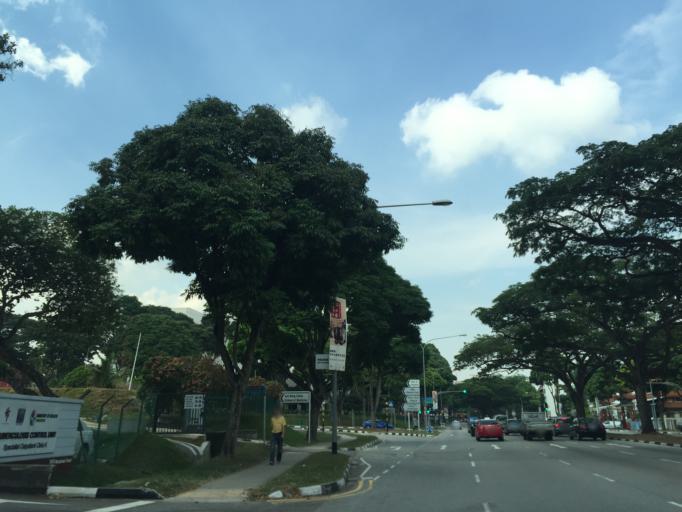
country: SG
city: Singapore
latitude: 1.3189
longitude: 103.8475
